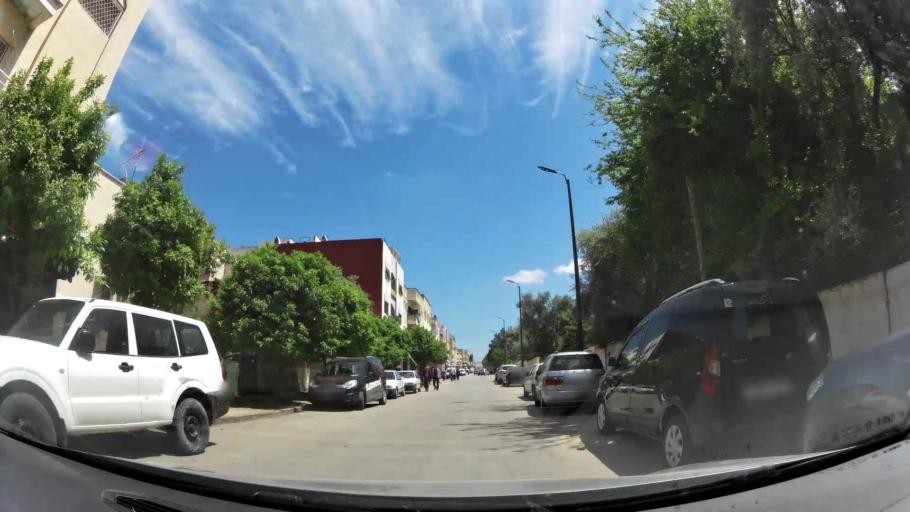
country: MA
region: Fes-Boulemane
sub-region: Fes
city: Fes
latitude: 34.0119
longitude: -4.9840
